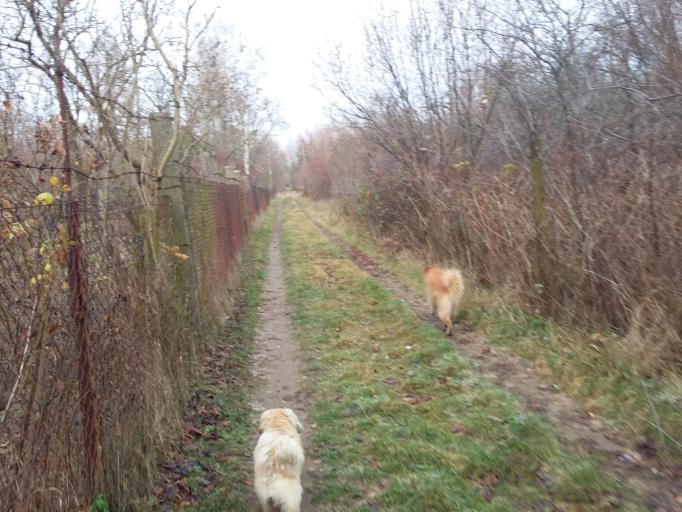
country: PL
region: Lodz Voivodeship
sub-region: Powiat pabianicki
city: Ksawerow
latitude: 51.7312
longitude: 19.4116
